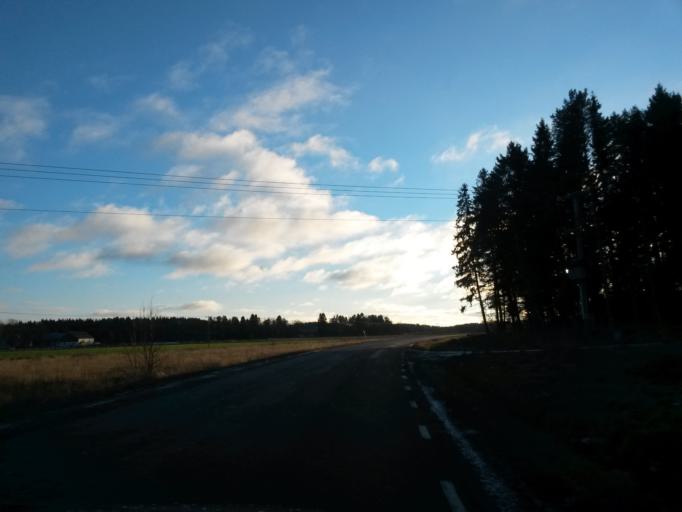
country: SE
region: Vaestra Goetaland
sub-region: Essunga Kommun
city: Nossebro
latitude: 58.2198
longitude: 12.7193
